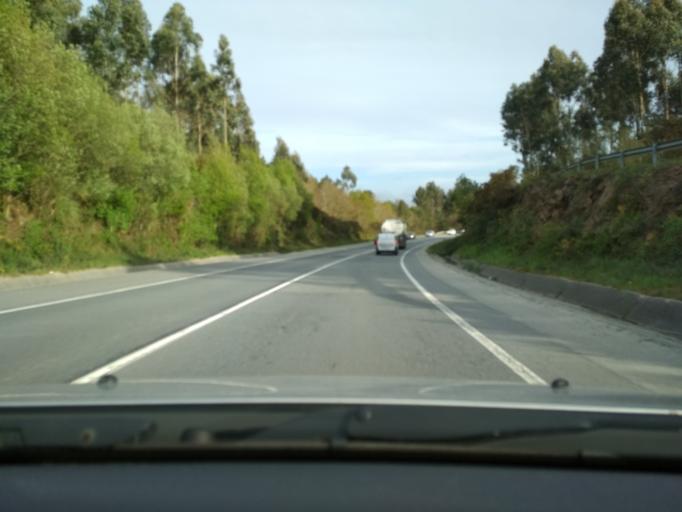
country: ES
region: Galicia
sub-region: Provincia da Coruna
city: Cerceda
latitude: 43.2236
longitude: -8.4593
